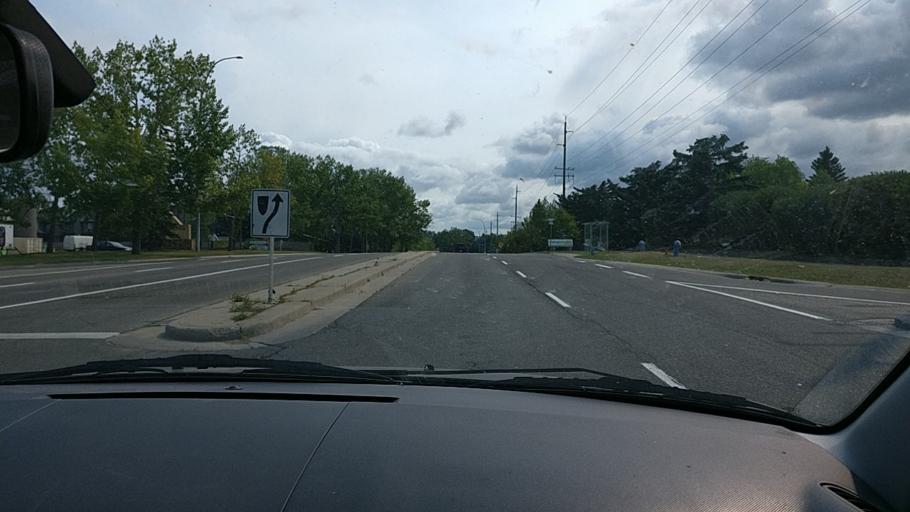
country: CA
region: Alberta
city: Calgary
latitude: 51.1035
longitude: -114.1892
